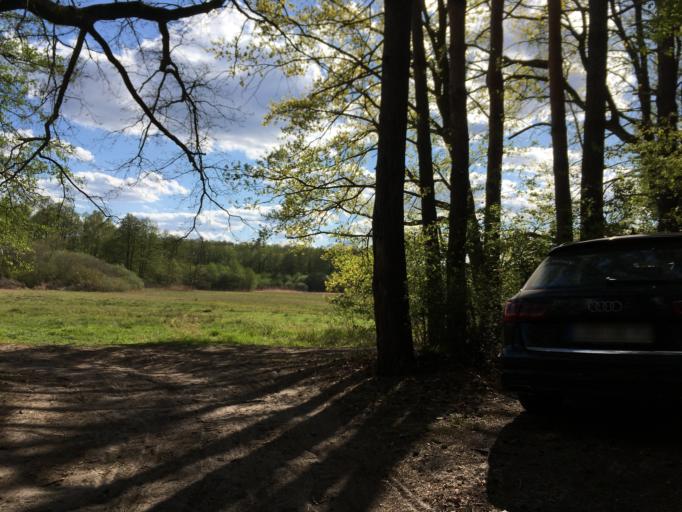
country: DE
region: Brandenburg
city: Wandlitz
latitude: 52.7515
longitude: 13.4332
